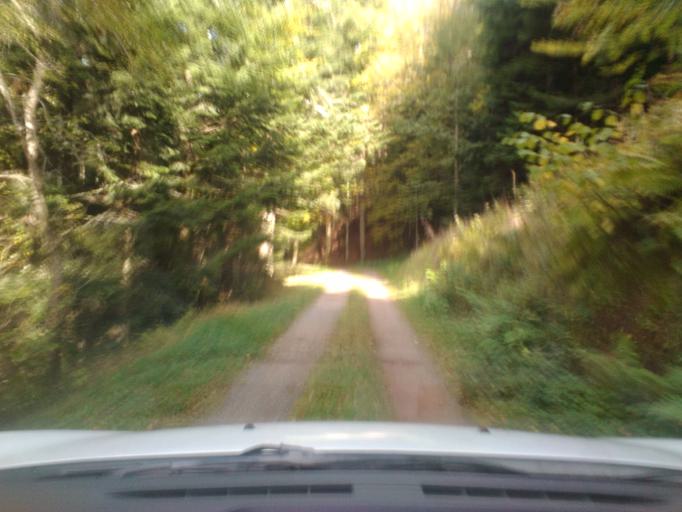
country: FR
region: Lorraine
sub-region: Departement des Vosges
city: Ban-de-Laveline
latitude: 48.3026
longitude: 7.0406
